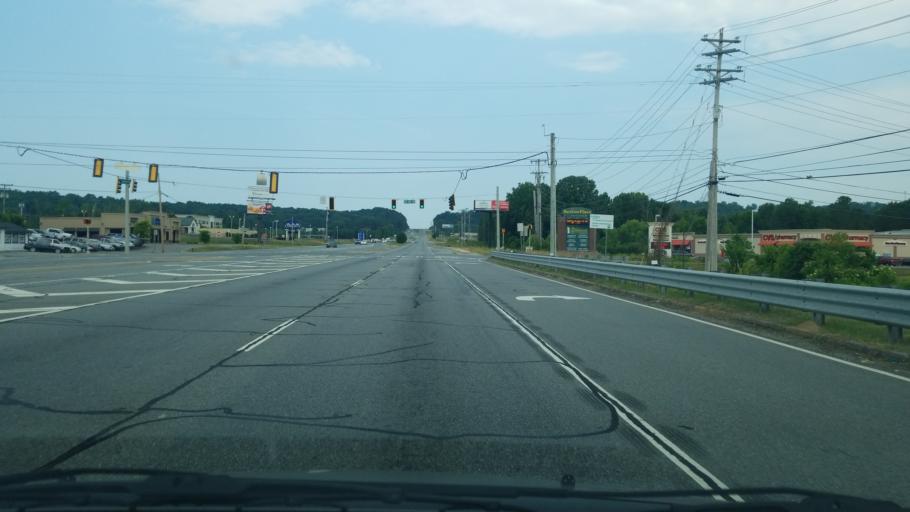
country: US
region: Georgia
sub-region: Catoosa County
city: Indian Springs
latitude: 34.9318
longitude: -85.1817
